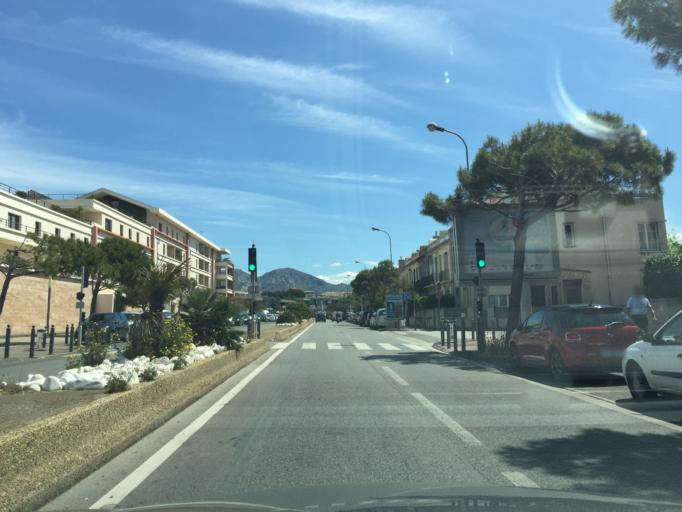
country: FR
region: Provence-Alpes-Cote d'Azur
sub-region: Departement des Bouches-du-Rhone
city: Marseille 08
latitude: 43.2544
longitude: 5.3795
